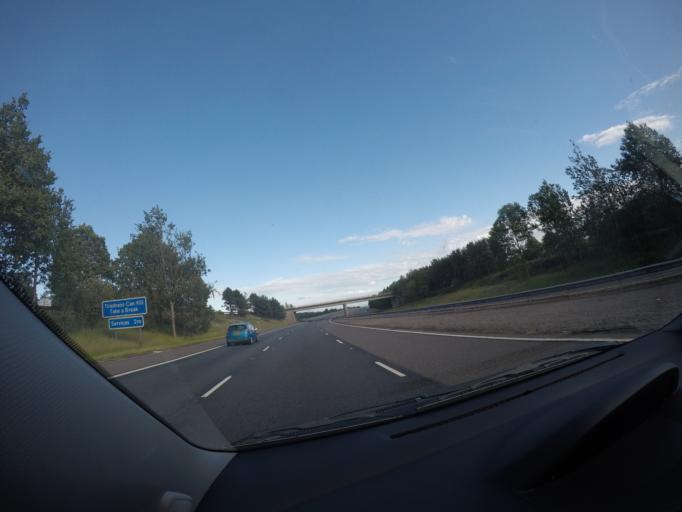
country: GB
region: Scotland
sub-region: Dumfries and Galloway
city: Gretna
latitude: 55.0260
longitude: -3.1299
